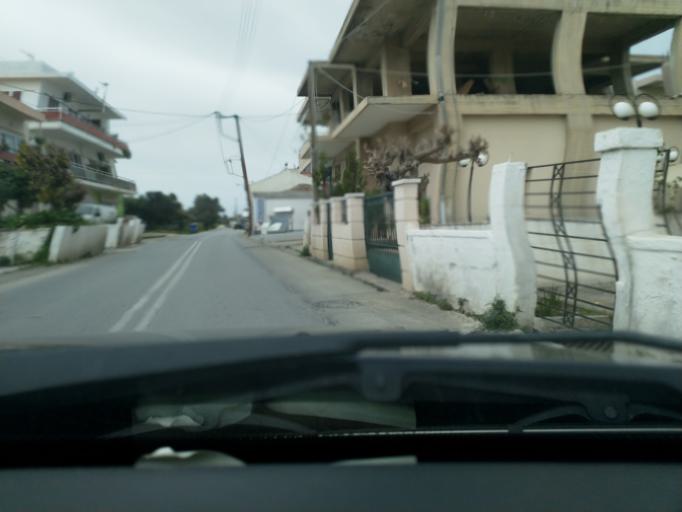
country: GR
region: Crete
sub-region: Nomos Chanias
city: Mournies
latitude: 35.4940
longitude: 24.0219
